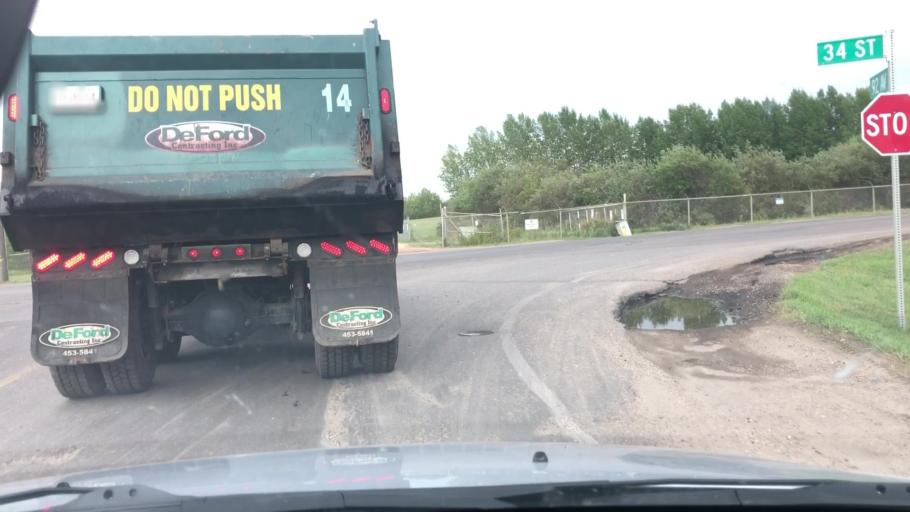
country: CA
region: Alberta
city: Sherwood Park
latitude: 53.5267
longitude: -113.3943
